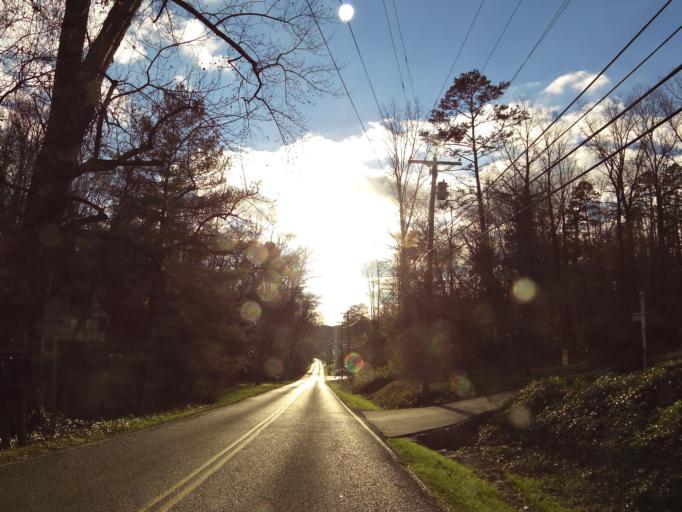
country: US
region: Tennessee
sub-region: Knox County
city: Knoxville
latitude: 35.9189
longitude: -83.9623
